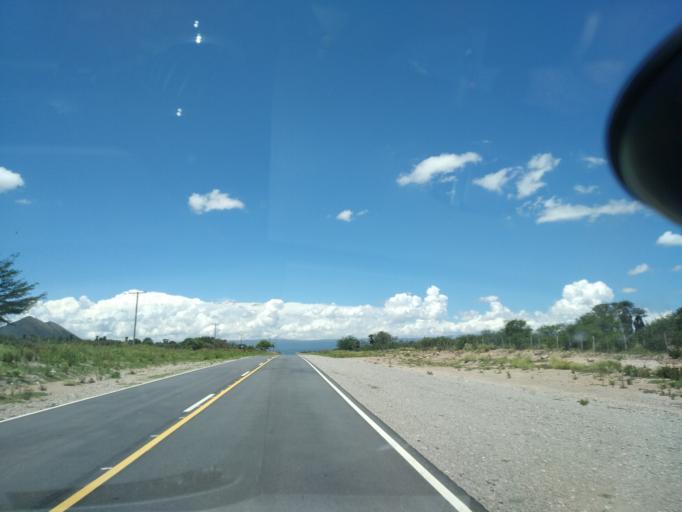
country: AR
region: Cordoba
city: Salsacate
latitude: -31.3613
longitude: -65.1883
